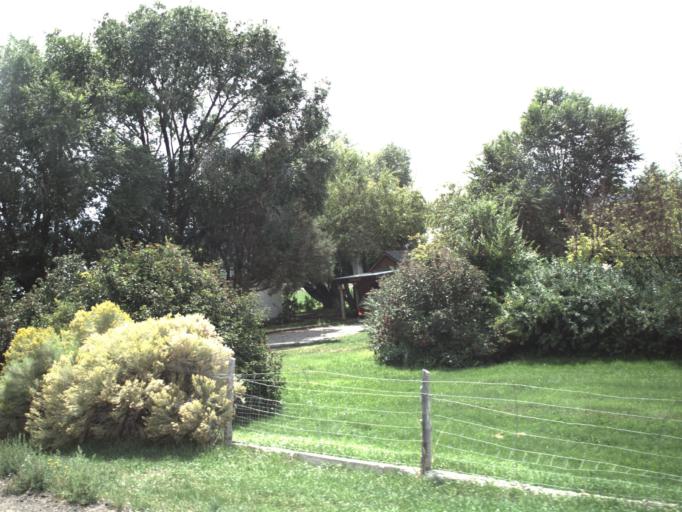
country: US
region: Utah
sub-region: Piute County
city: Junction
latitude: 38.1251
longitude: -112.0005
